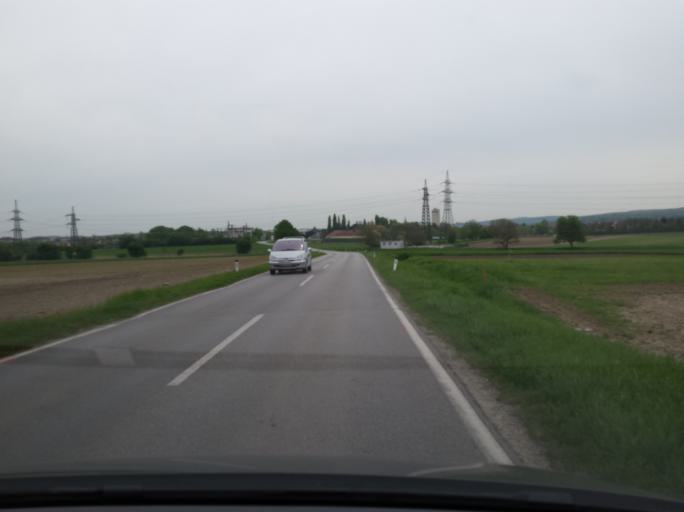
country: AT
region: Lower Austria
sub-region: Politischer Bezirk Bruck an der Leitha
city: Bruck an der Leitha
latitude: 48.0356
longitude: 16.7619
